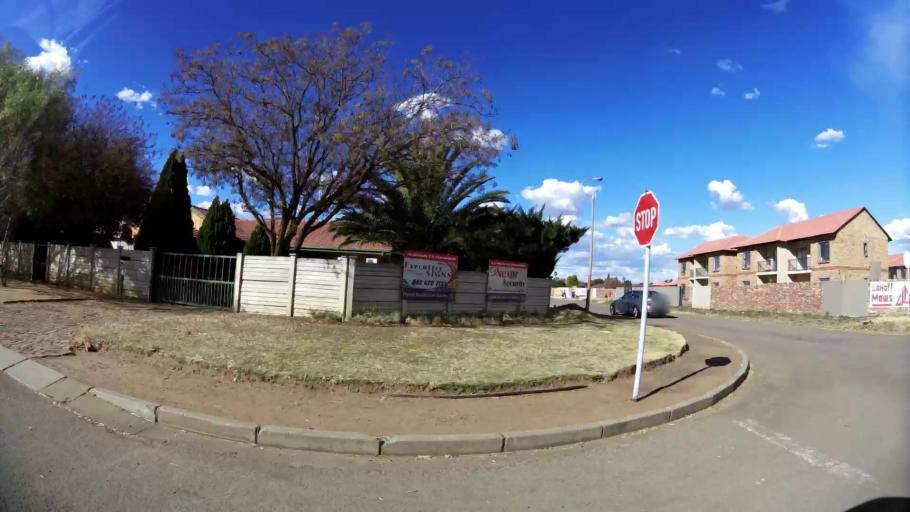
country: ZA
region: North-West
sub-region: Dr Kenneth Kaunda District Municipality
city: Klerksdorp
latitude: -26.8221
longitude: 26.6575
